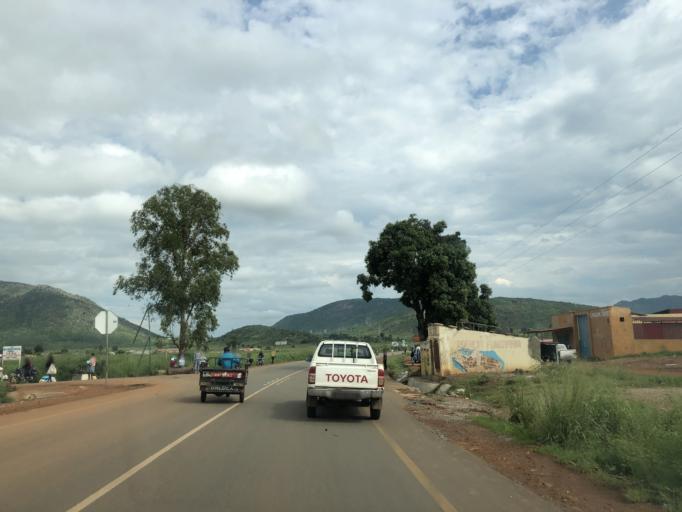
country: AO
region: Cuanza Sul
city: Uacu Cungo
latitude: -11.3478
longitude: 15.1048
